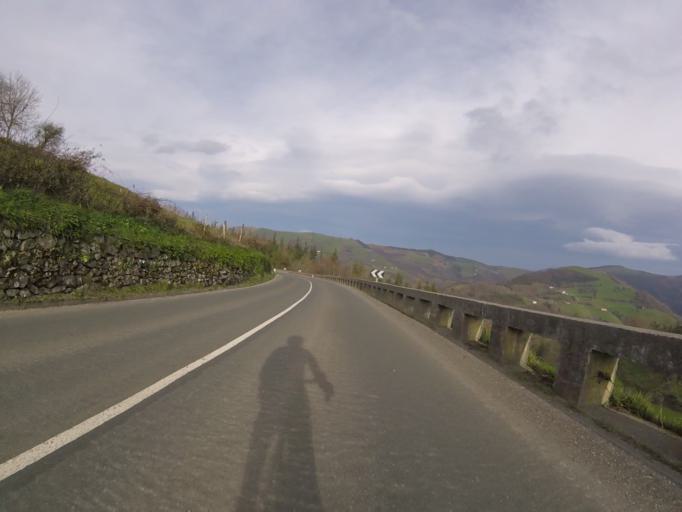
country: ES
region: Basque Country
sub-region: Provincia de Guipuzcoa
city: Beizama
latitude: 43.1675
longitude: -2.2218
